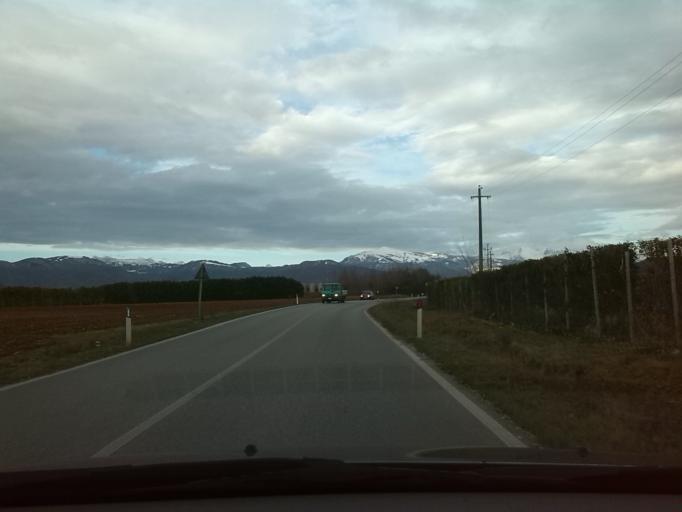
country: IT
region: Friuli Venezia Giulia
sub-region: Provincia di Udine
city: Premariacco
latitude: 46.0542
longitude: 13.4116
